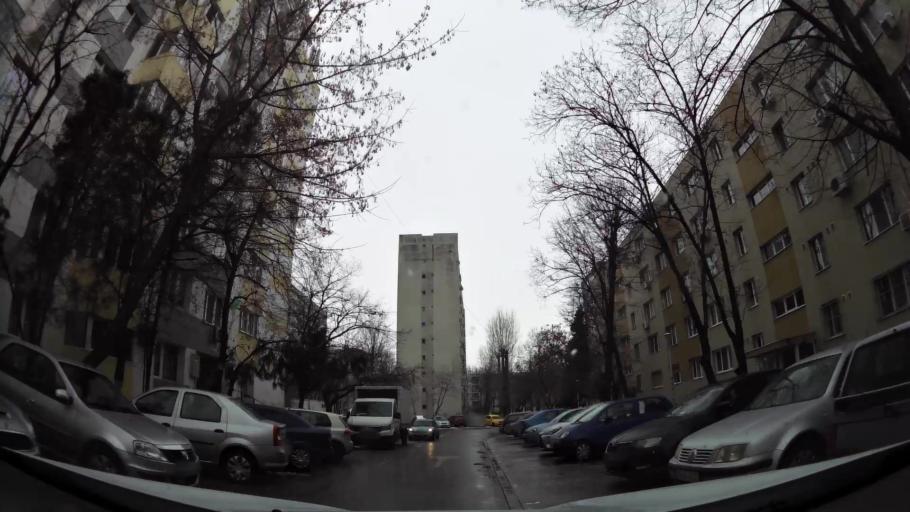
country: RO
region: Ilfov
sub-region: Comuna Chiajna
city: Rosu
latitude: 44.4162
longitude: 26.0305
